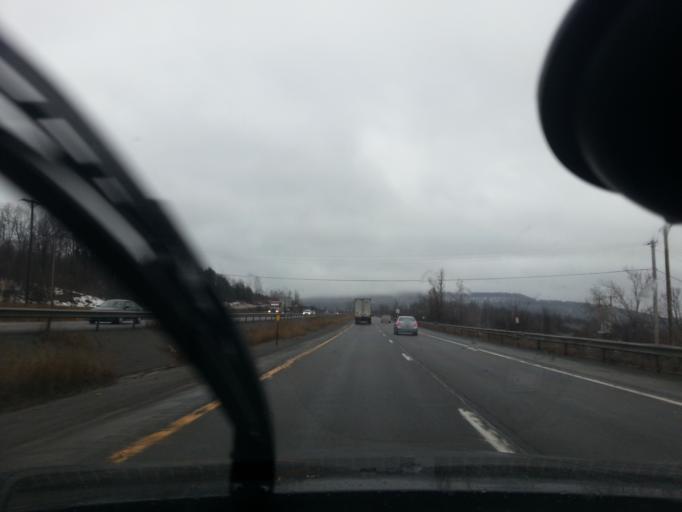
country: US
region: New York
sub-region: Onondaga County
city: Nedrow
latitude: 42.9534
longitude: -76.1383
